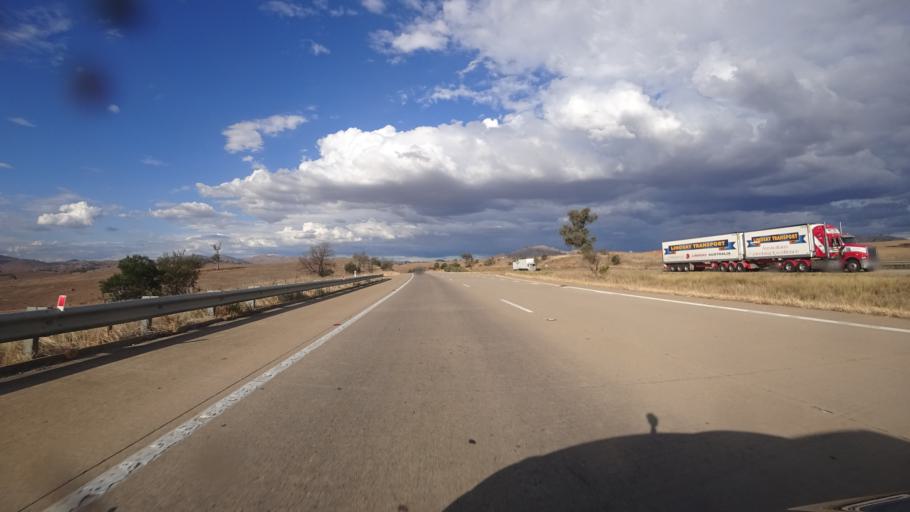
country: AU
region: New South Wales
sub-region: Gundagai
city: Gundagai
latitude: -34.8157
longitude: 148.4429
